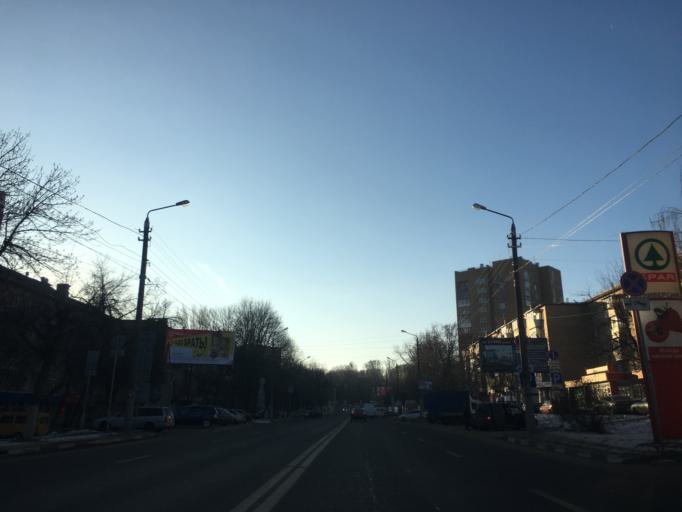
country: RU
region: Tula
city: Tula
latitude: 54.1885
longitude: 37.5923
